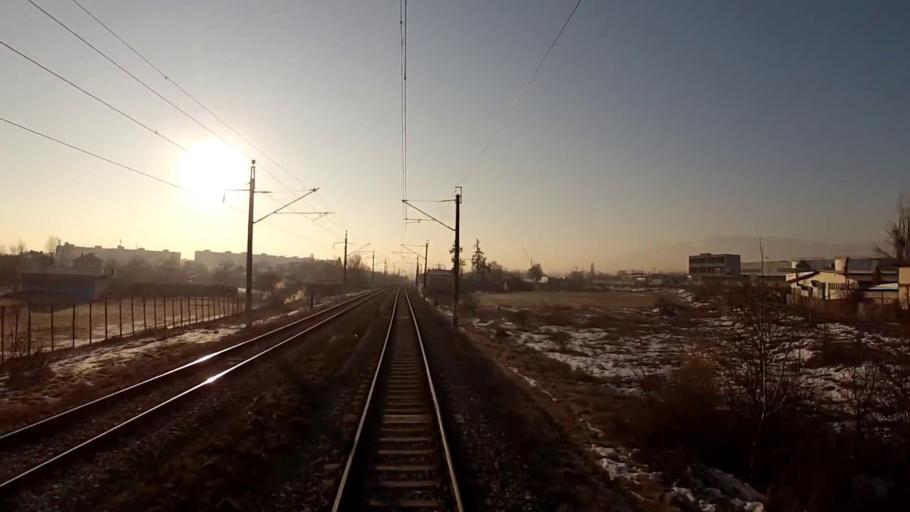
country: BG
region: Sofiya
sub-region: Obshtina Bozhurishte
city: Bozhurishte
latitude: 42.7479
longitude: 23.2530
